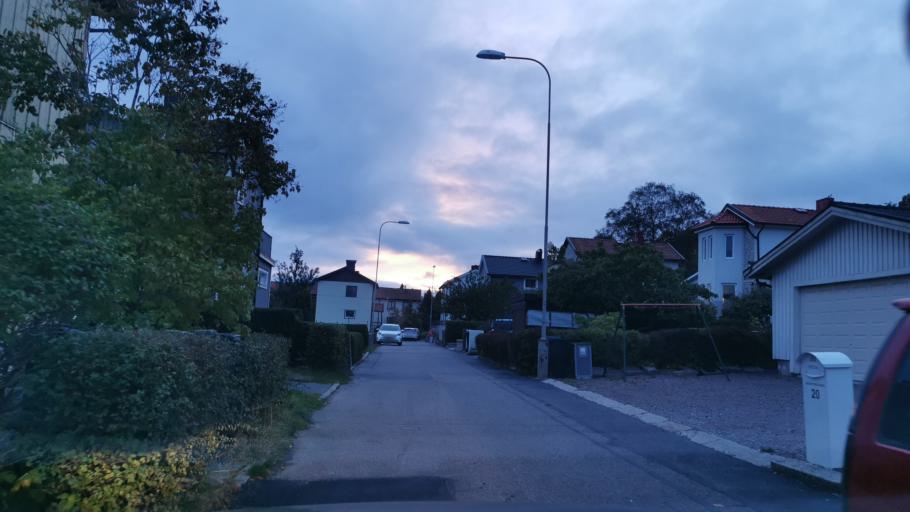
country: SE
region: Vaestra Goetaland
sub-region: Goteborg
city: Eriksbo
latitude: 57.7361
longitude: 12.0574
